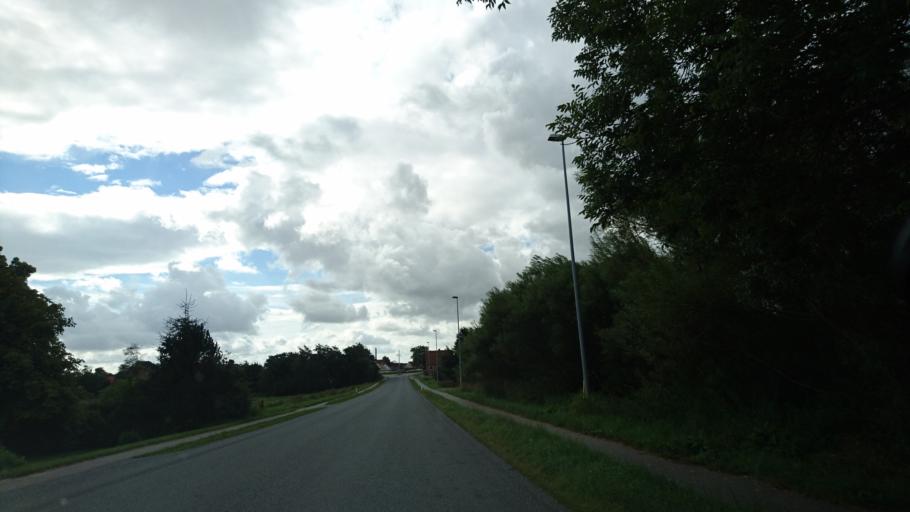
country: DK
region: North Denmark
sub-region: Hjorring Kommune
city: Tars
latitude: 57.3467
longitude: 10.2307
